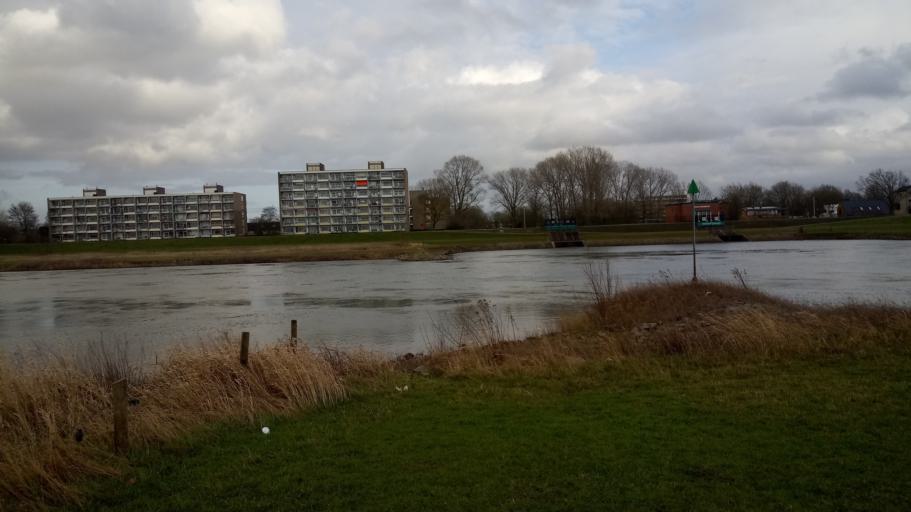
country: NL
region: Gelderland
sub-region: Gemeente Zutphen
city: Zutphen
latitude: 52.1333
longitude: 6.1900
